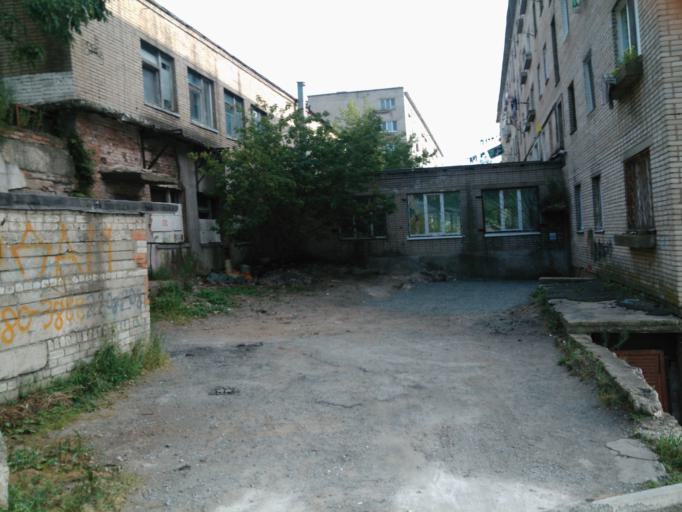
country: RU
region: Primorskiy
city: Vladivostok
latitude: 43.0917
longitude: 131.9601
